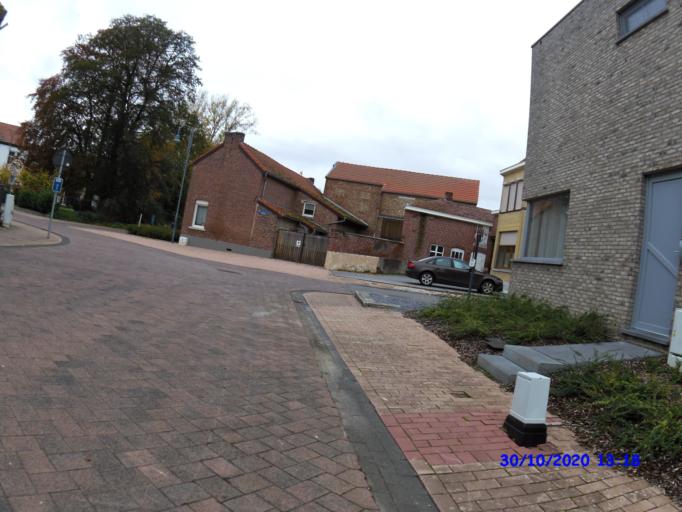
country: BE
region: Flanders
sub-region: Provincie Limburg
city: Gingelom
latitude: 50.7422
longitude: 5.1826
